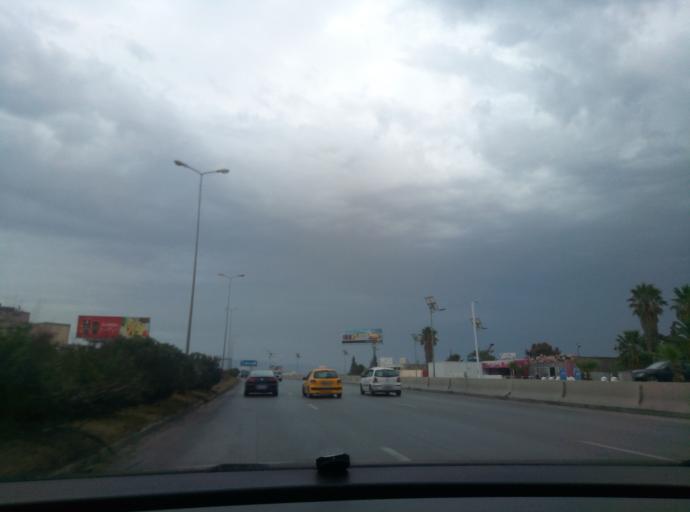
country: TN
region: Bin 'Arus
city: Ben Arous
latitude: 36.7338
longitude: 10.2248
